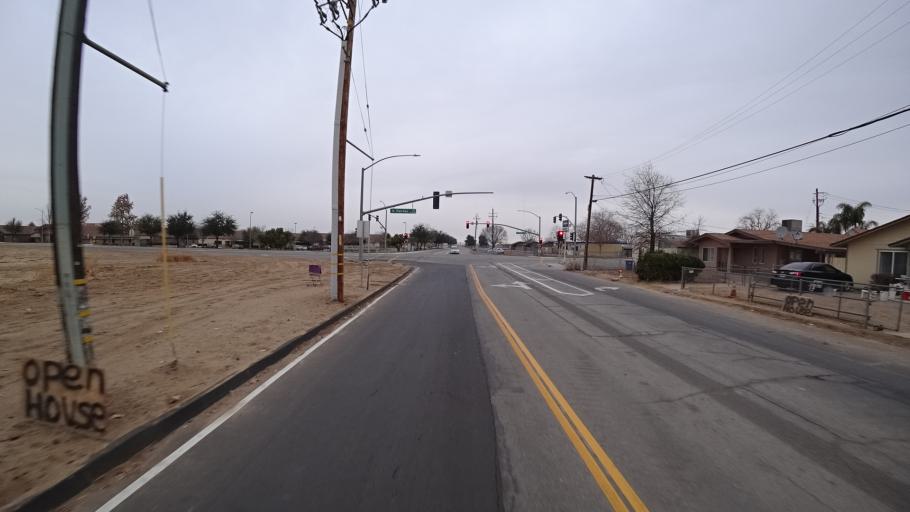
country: US
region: California
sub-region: Kern County
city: Lamont
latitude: 35.3397
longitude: -118.9314
